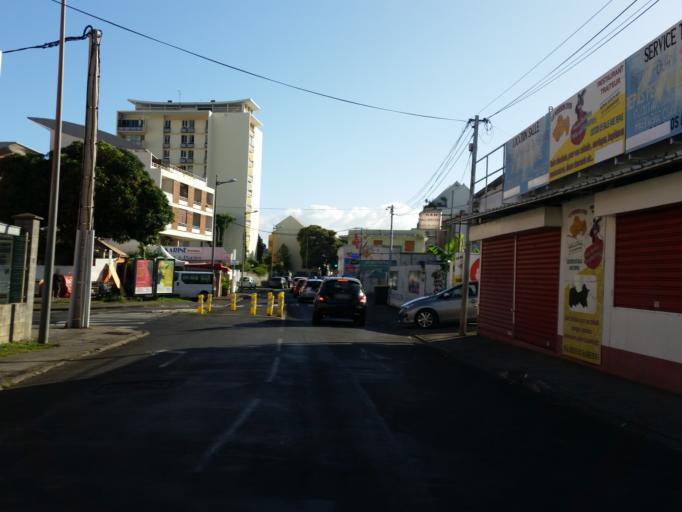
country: RE
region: Reunion
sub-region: Reunion
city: Saint-Denis
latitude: -20.8896
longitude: 55.4550
